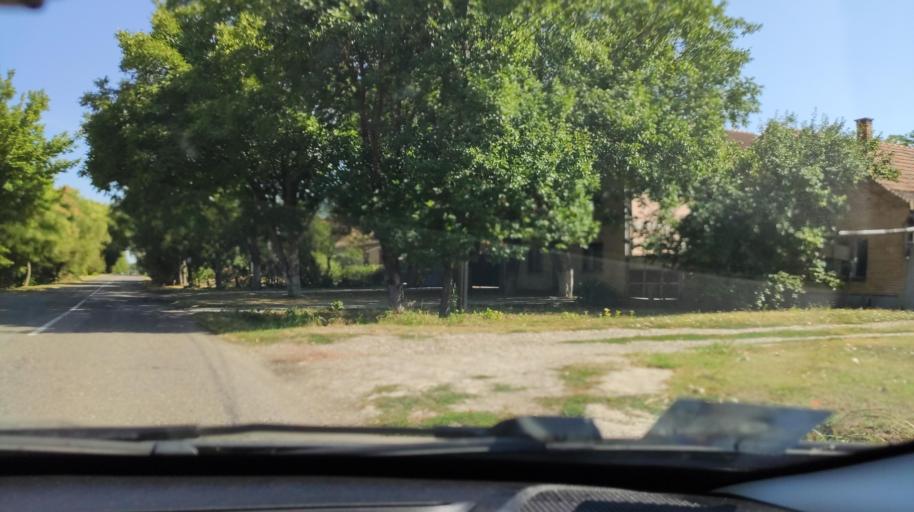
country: RS
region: Autonomna Pokrajina Vojvodina
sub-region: Severnobacki Okrug
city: Backa Topola
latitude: 45.8202
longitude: 19.6222
